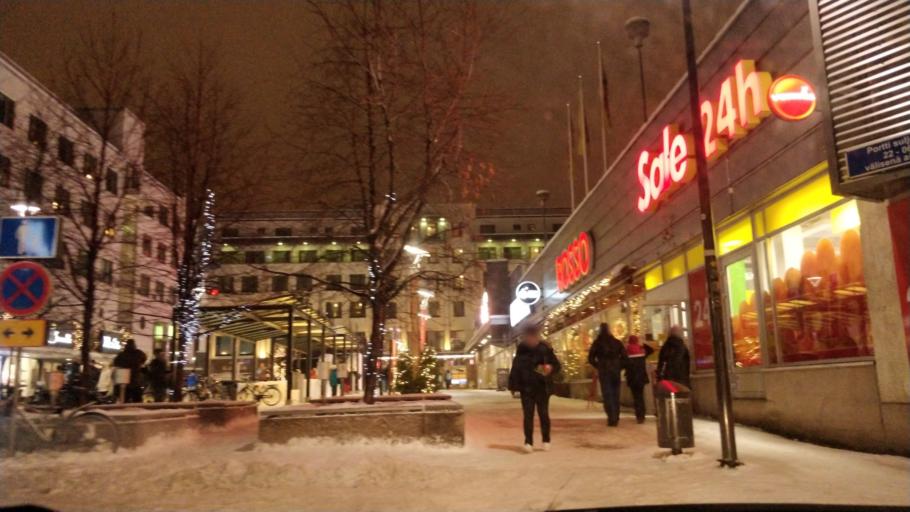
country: FI
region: Lapland
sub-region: Rovaniemi
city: Rovaniemi
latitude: 66.5017
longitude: 25.7301
